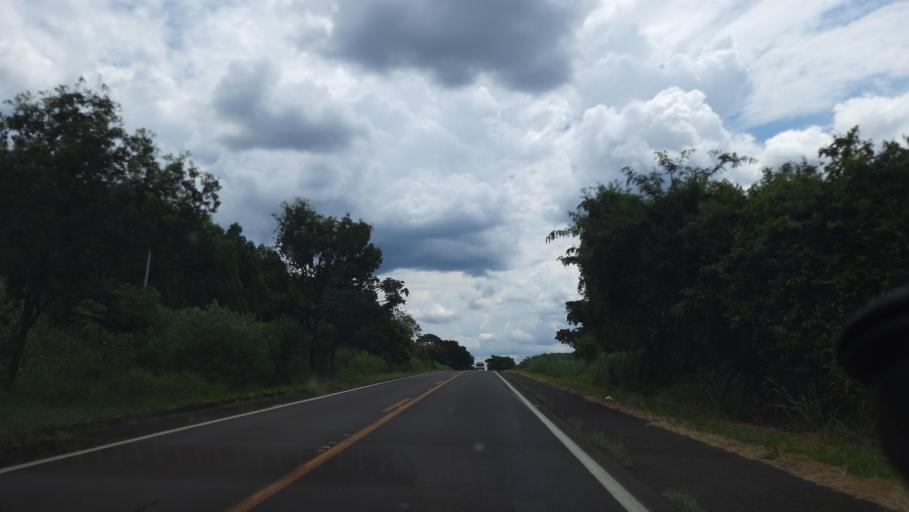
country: BR
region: Sao Paulo
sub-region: Mococa
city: Mococa
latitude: -21.4601
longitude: -47.1128
